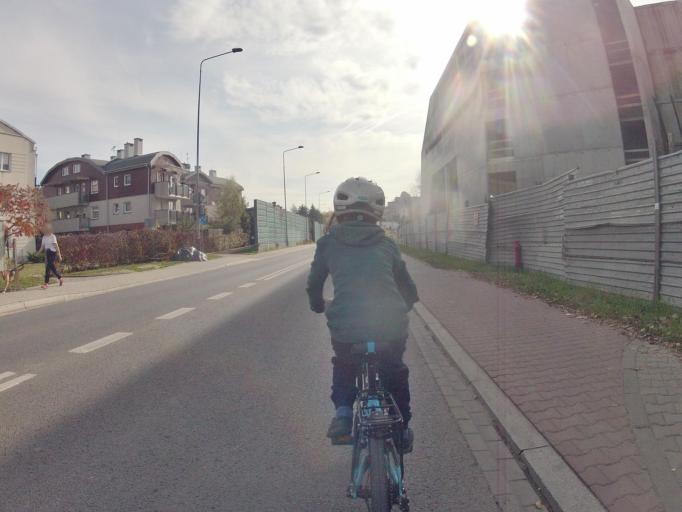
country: PL
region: Lesser Poland Voivodeship
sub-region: Krakow
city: Krakow
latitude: 50.0318
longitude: 19.9116
